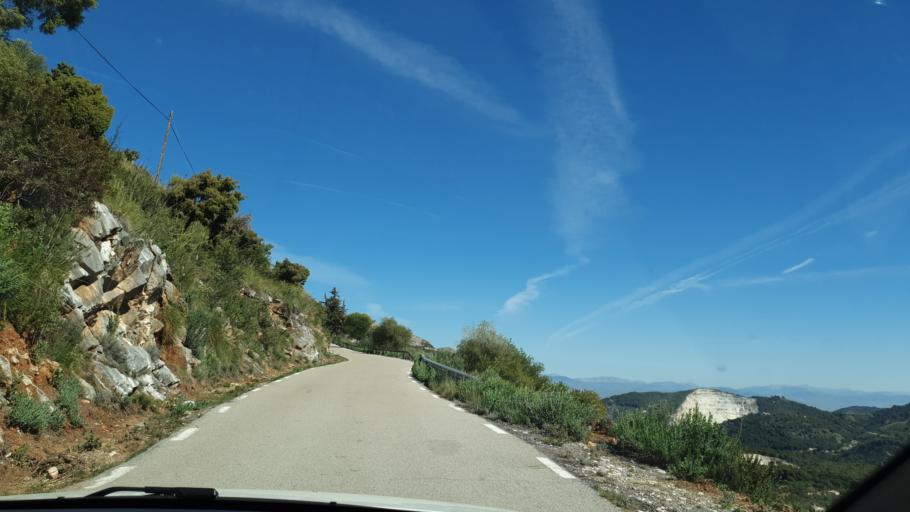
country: ES
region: Andalusia
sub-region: Provincia de Malaga
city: Ojen
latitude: 36.5882
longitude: -4.8721
